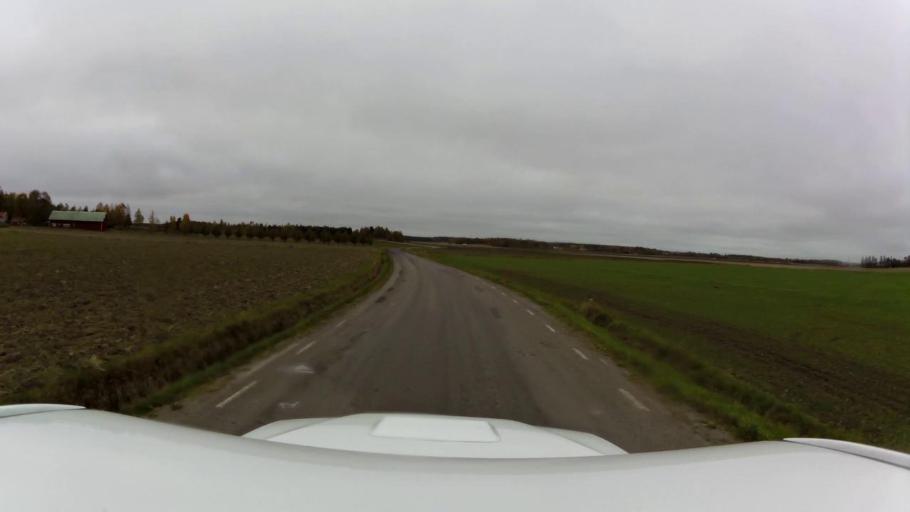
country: SE
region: OEstergoetland
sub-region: Linkopings Kommun
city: Linghem
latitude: 58.4485
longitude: 15.7111
